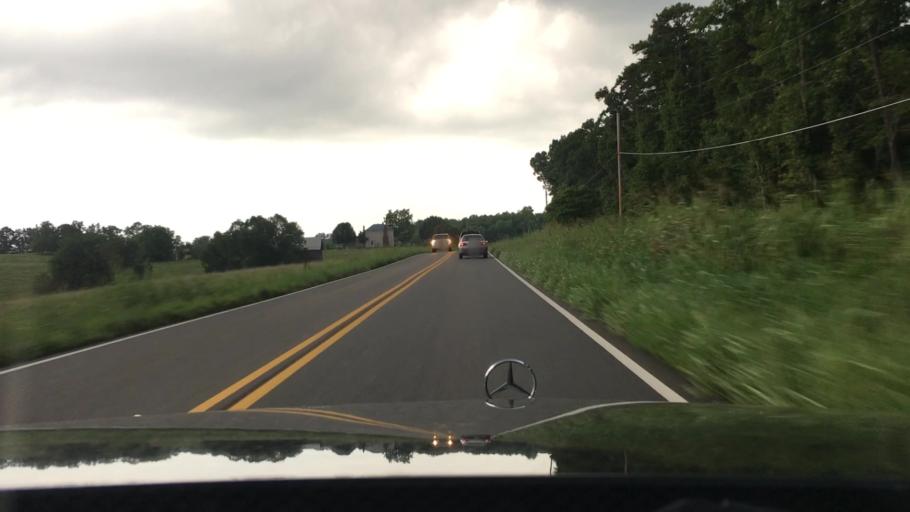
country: US
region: Virginia
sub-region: Campbell County
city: Timberlake
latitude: 37.2902
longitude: -79.2369
